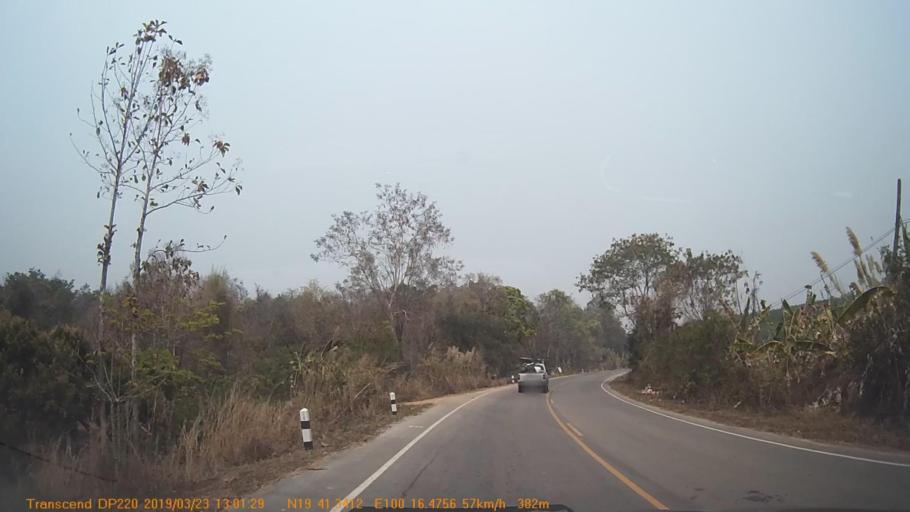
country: TH
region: Chiang Rai
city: Thoeng
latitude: 19.6893
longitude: 100.2746
